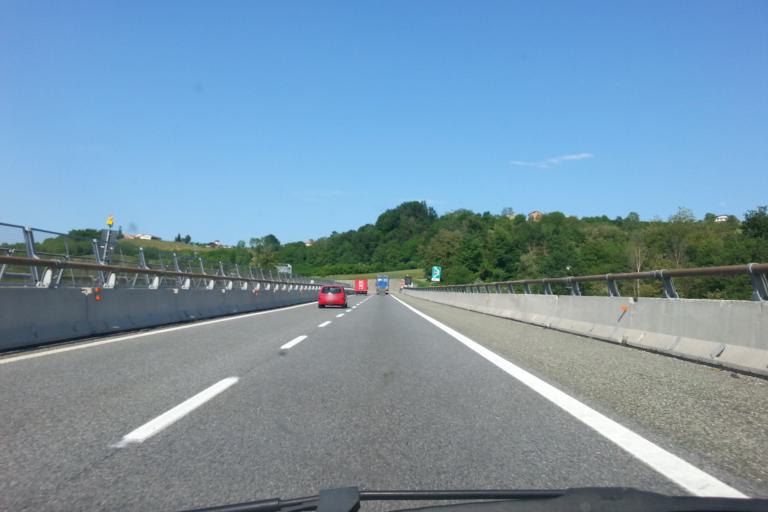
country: IT
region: Piedmont
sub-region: Provincia di Cuneo
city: Briaglia
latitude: 44.4175
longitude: 7.8674
